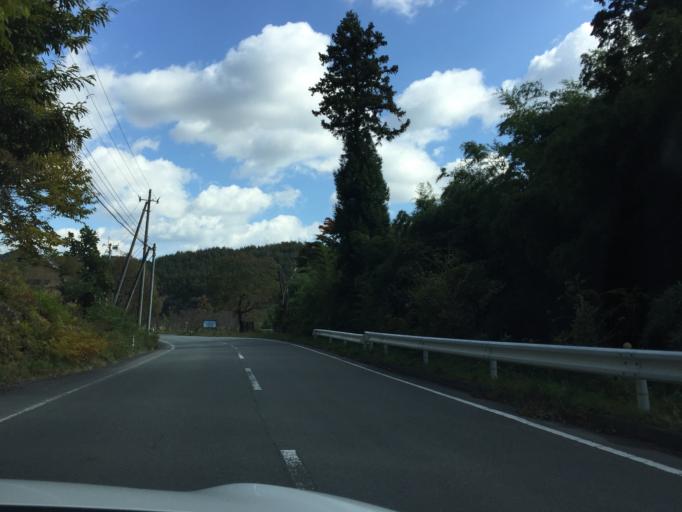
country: JP
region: Fukushima
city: Funehikimachi-funehiki
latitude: 37.3297
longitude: 140.7898
